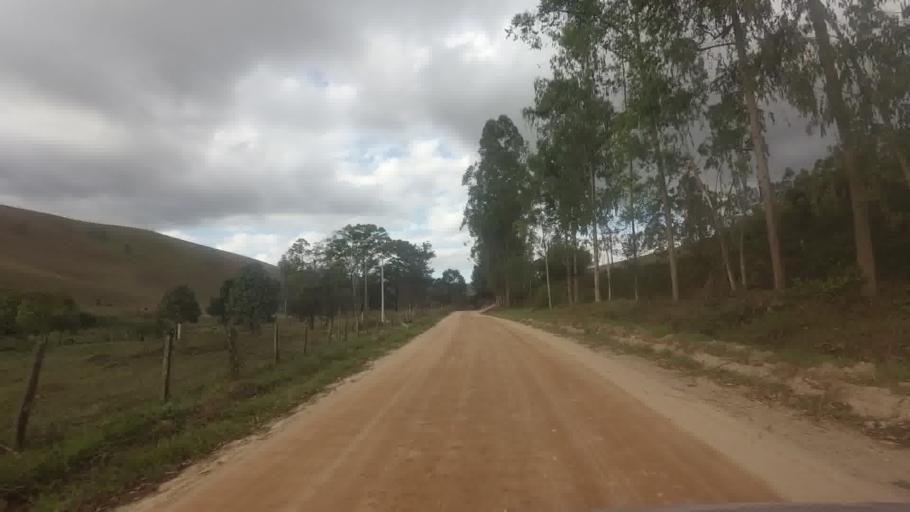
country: BR
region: Espirito Santo
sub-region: Mimoso Do Sul
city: Mimoso do Sul
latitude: -20.9538
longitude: -41.4266
